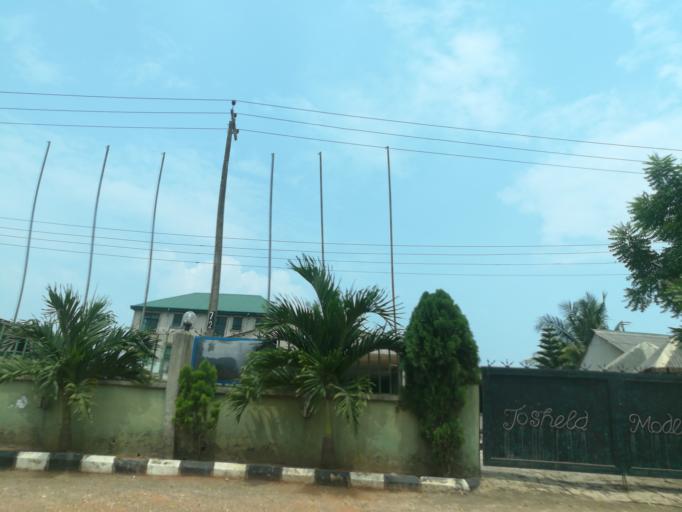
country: NG
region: Lagos
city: Ikorodu
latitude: 6.6048
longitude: 3.5864
